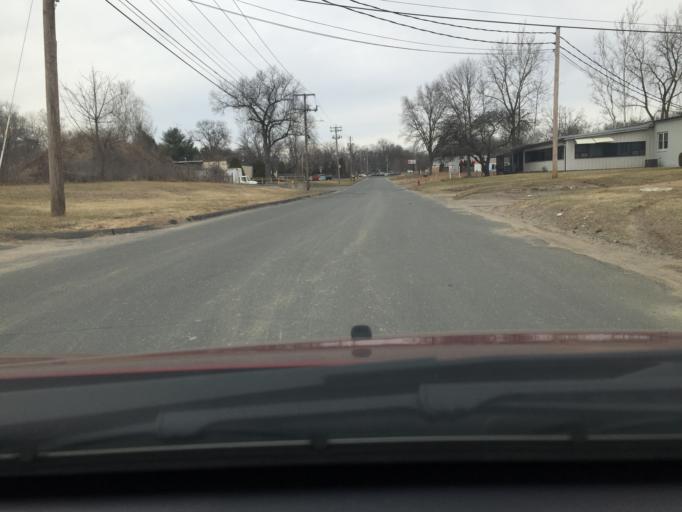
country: US
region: Massachusetts
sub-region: Hampden County
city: Westfield
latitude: 42.1127
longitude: -72.7317
